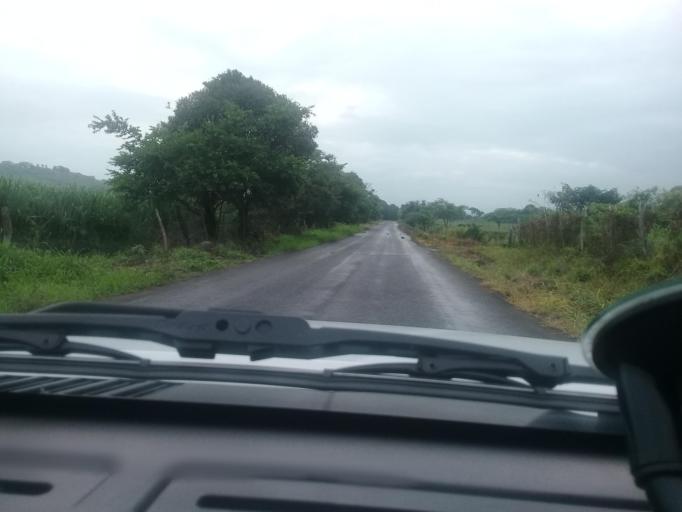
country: MX
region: Veracruz
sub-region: Paso de Ovejas
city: Tolome
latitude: 19.2578
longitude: -96.4232
